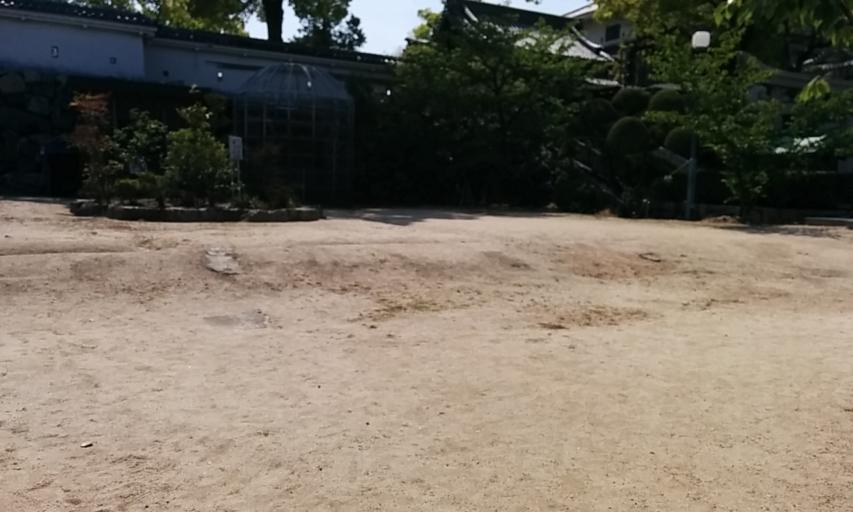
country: JP
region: Ehime
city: Saijo
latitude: 34.0632
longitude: 133.0076
